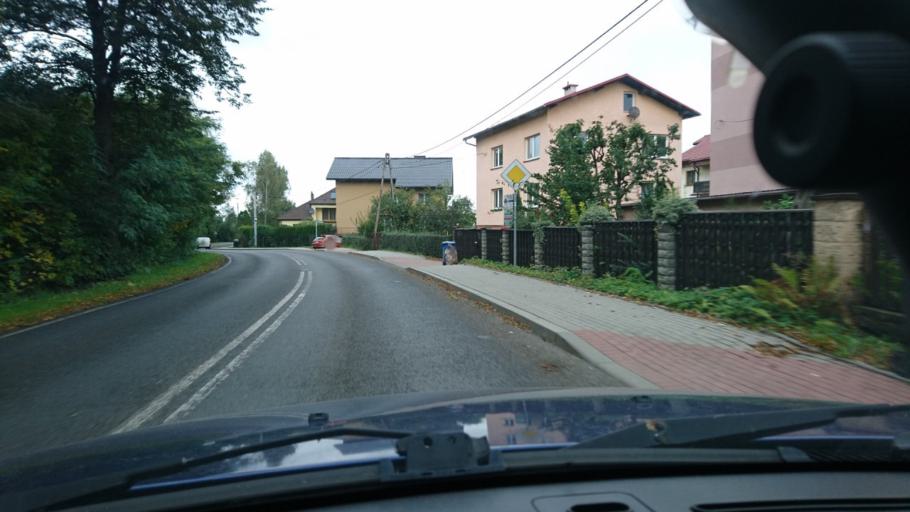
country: PL
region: Silesian Voivodeship
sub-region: Powiat bielski
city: Jaworze
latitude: 49.7994
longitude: 18.9847
